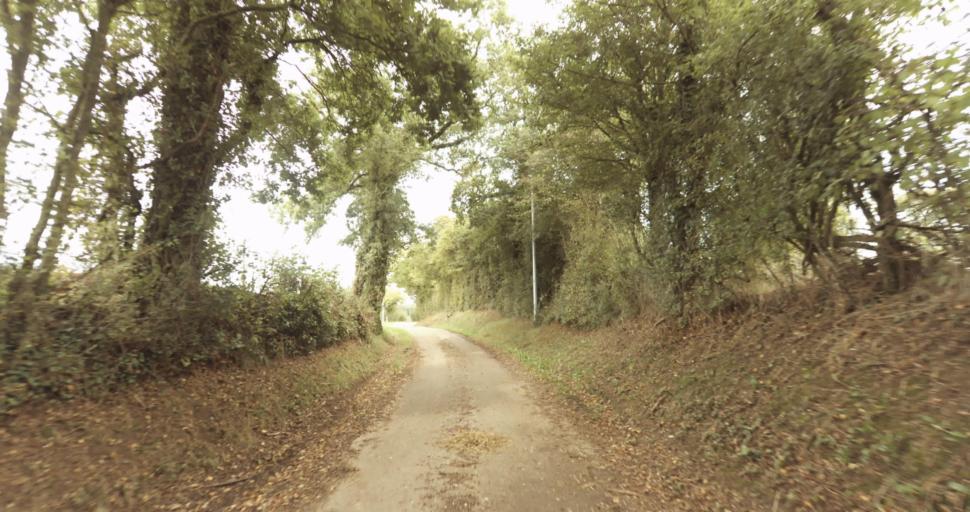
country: FR
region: Lower Normandy
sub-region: Departement de l'Orne
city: Gace
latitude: 48.6845
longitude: 0.2891
